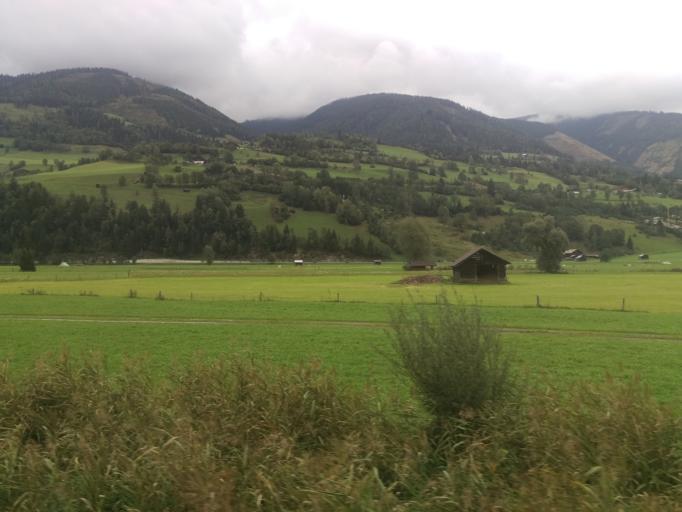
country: AT
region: Salzburg
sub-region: Politischer Bezirk Zell am See
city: Niedernsill
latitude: 47.2803
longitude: 12.6153
